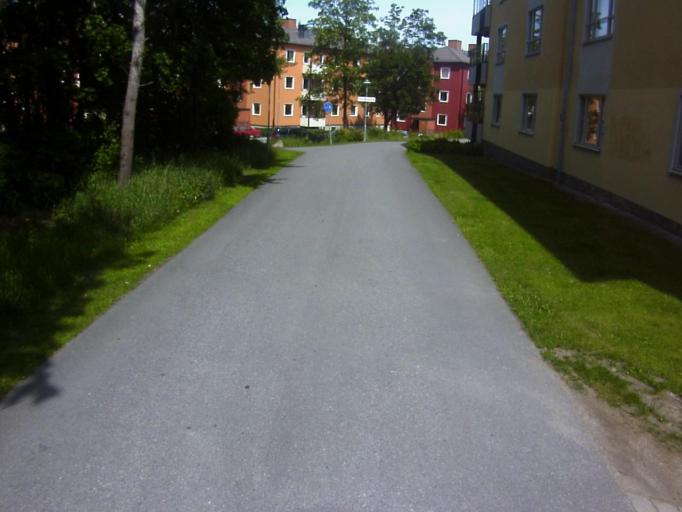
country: SE
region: Soedermanland
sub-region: Eskilstuna Kommun
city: Eskilstuna
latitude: 59.3578
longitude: 16.5252
